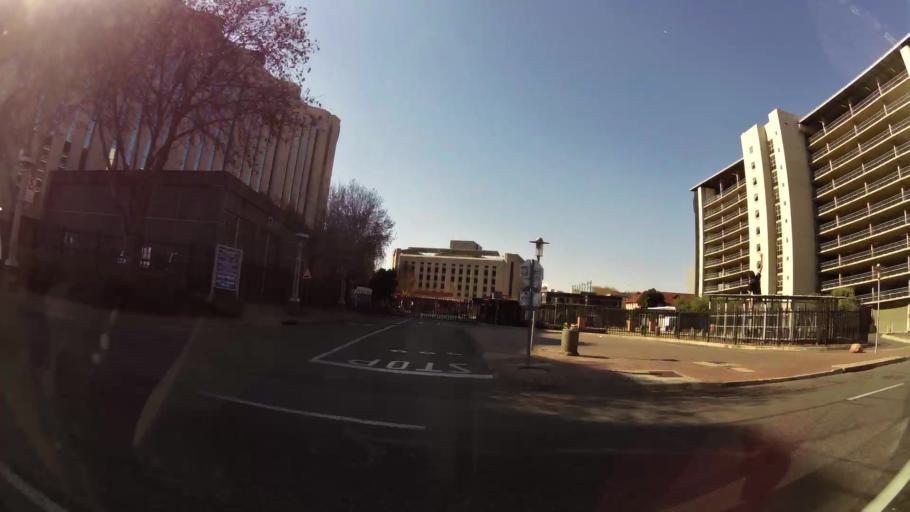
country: ZA
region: Gauteng
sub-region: City of Johannesburg Metropolitan Municipality
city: Johannesburg
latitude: -26.2107
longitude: 28.0387
